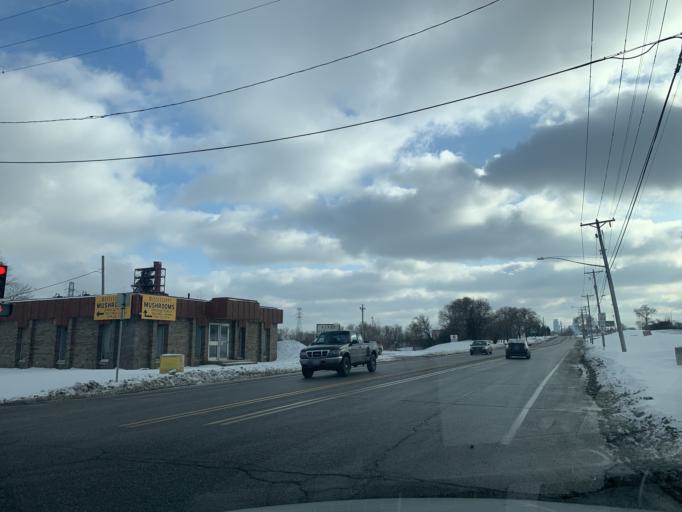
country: US
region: Minnesota
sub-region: Anoka County
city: Columbia Heights
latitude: 45.0239
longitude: -93.2827
